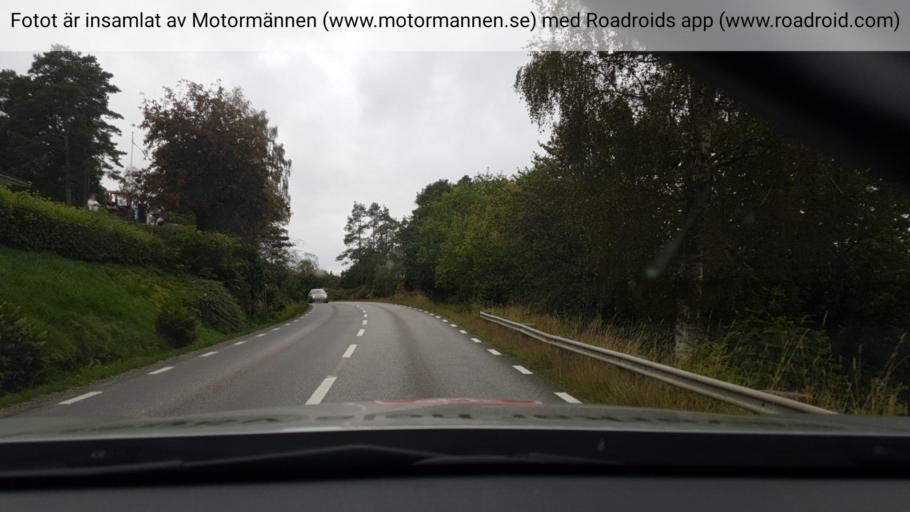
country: SE
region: Vaestra Goetaland
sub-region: Tanums Kommun
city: Grebbestad
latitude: 58.7226
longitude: 11.2870
